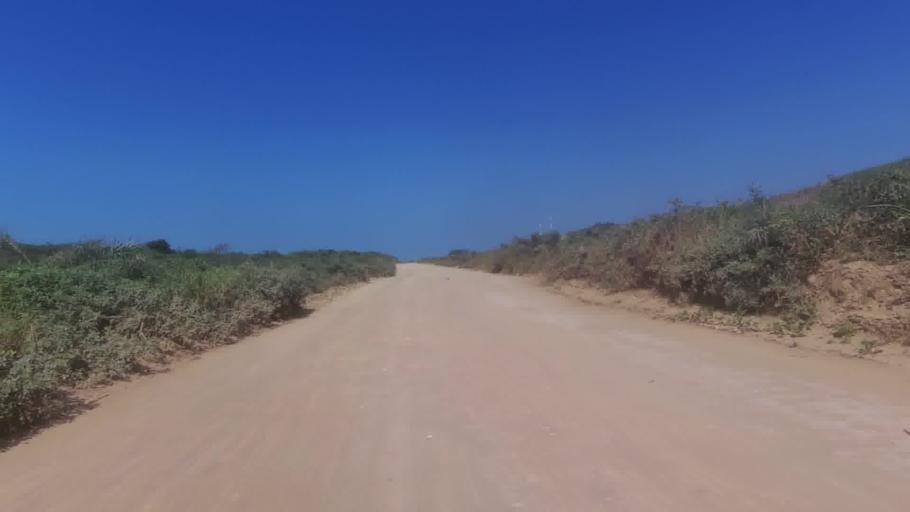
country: BR
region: Espirito Santo
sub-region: Marataizes
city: Marataizes
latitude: -21.0948
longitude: -40.8461
